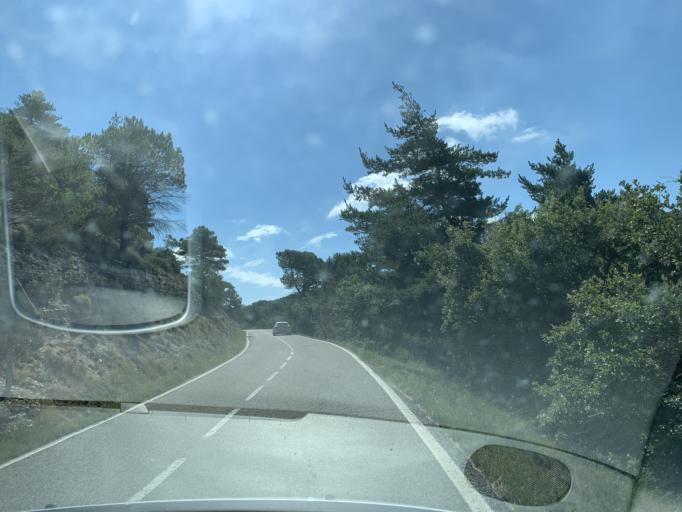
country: ES
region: Catalonia
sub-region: Provincia de Tarragona
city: Conesa
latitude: 41.5429
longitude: 1.3289
